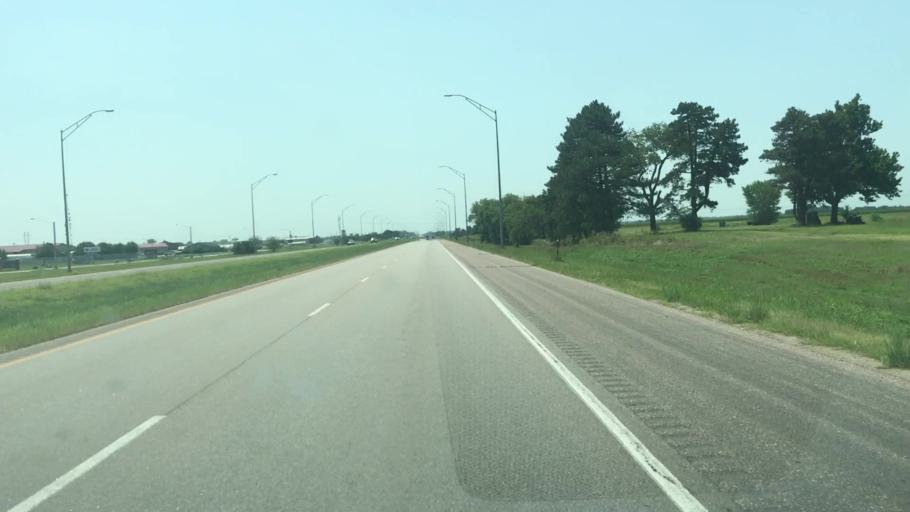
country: US
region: Nebraska
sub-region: Hall County
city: Grand Island
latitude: 40.8719
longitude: -98.3783
